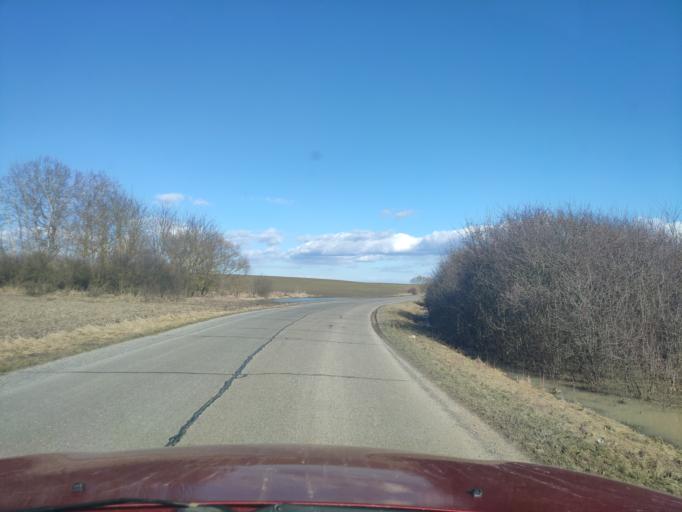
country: SK
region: Banskobystricky
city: Rimavska Sobota
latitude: 48.2850
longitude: 20.1279
